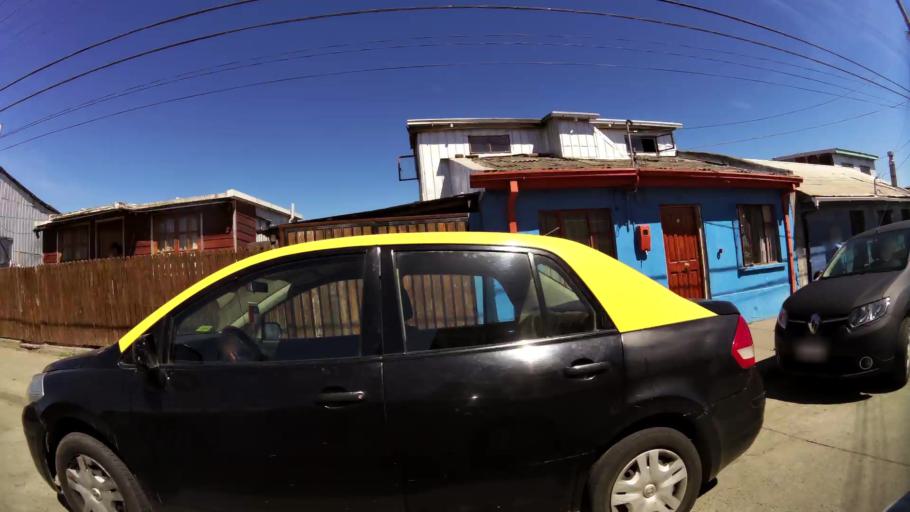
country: CL
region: Biobio
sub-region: Provincia de Concepcion
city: Penco
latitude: -36.7333
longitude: -72.9903
